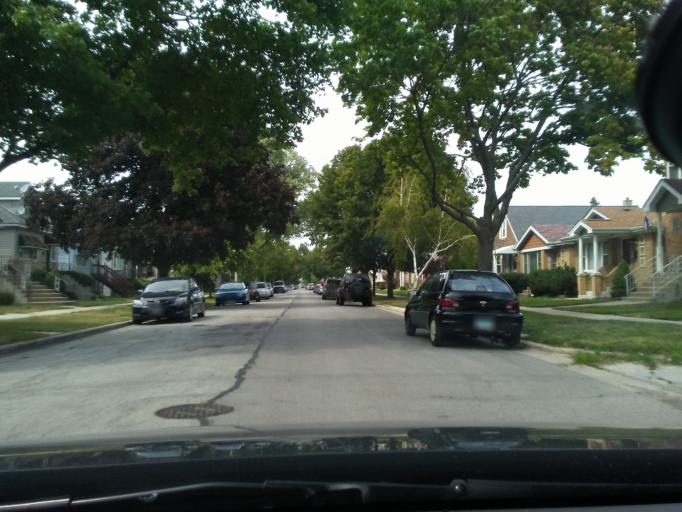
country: US
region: Illinois
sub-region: Cook County
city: Harwood Heights
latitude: 41.9761
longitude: -87.7836
